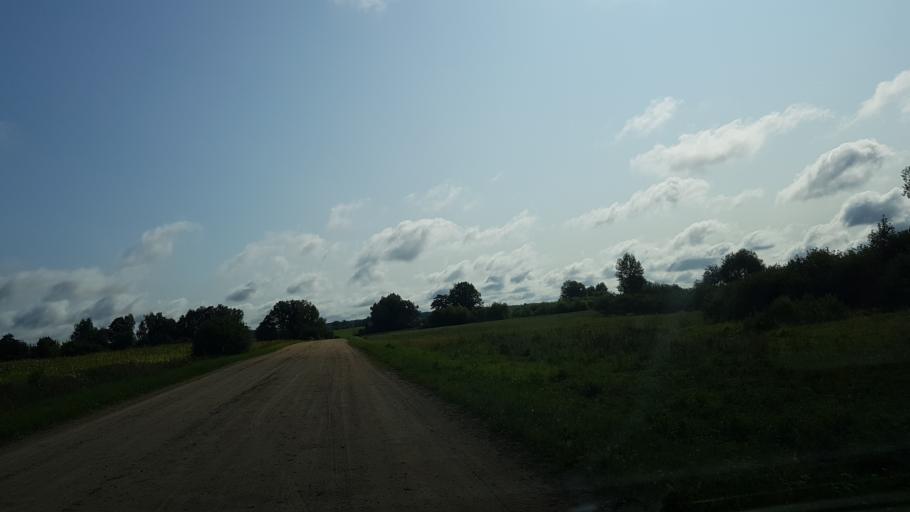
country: BY
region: Vitebsk
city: Dubrowna
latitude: 54.4805
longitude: 30.7793
